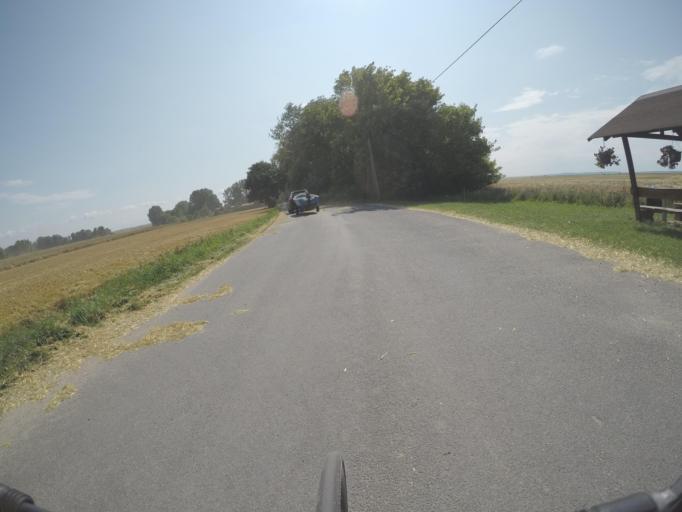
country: DE
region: Mecklenburg-Vorpommern
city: Gingst
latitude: 54.4372
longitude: 13.1758
